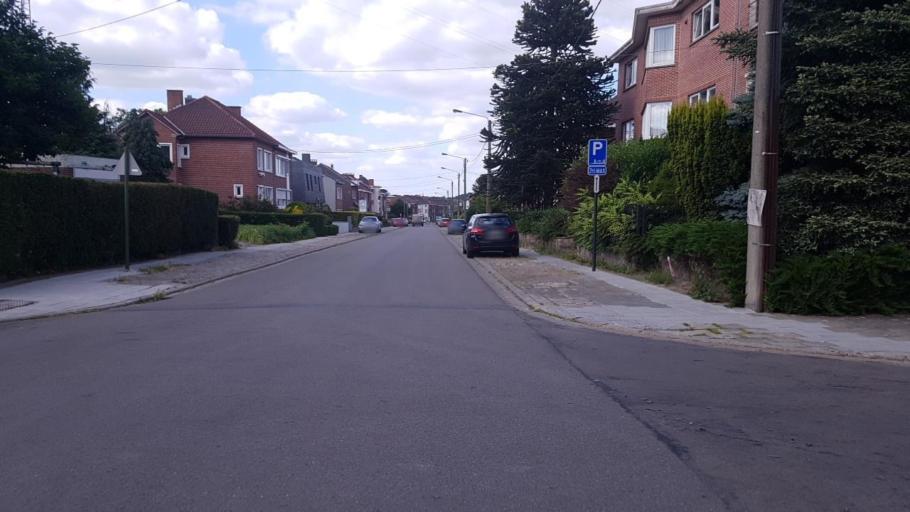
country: BE
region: Wallonia
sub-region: Province du Hainaut
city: Charleroi
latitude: 50.3879
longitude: 4.4563
